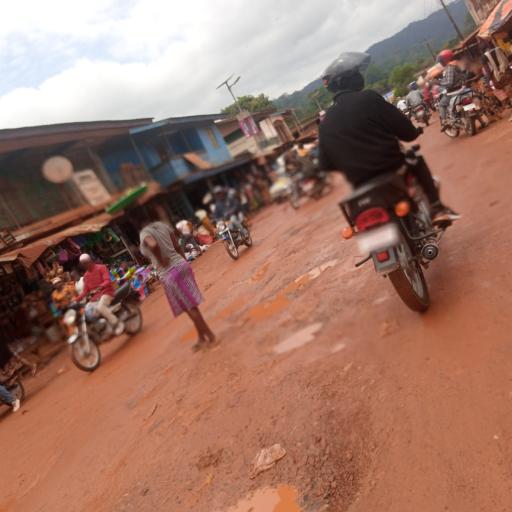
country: SL
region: Eastern Province
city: Kenema
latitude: 7.8753
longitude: -11.1930
